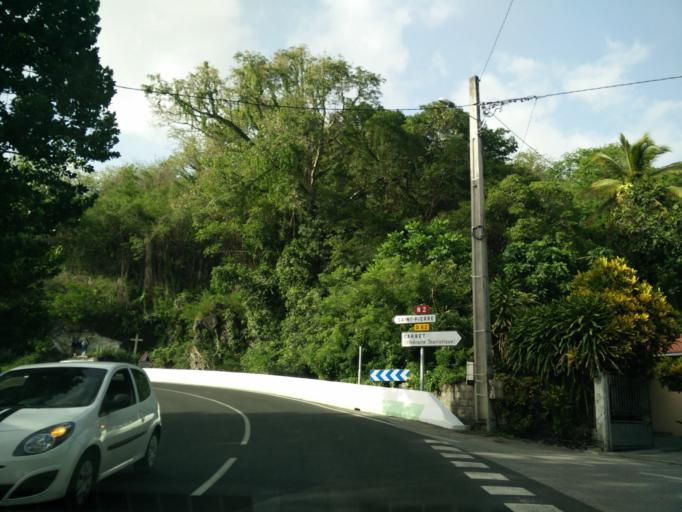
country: MQ
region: Martinique
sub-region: Martinique
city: Saint-Pierre
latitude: 14.7323
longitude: -61.1787
